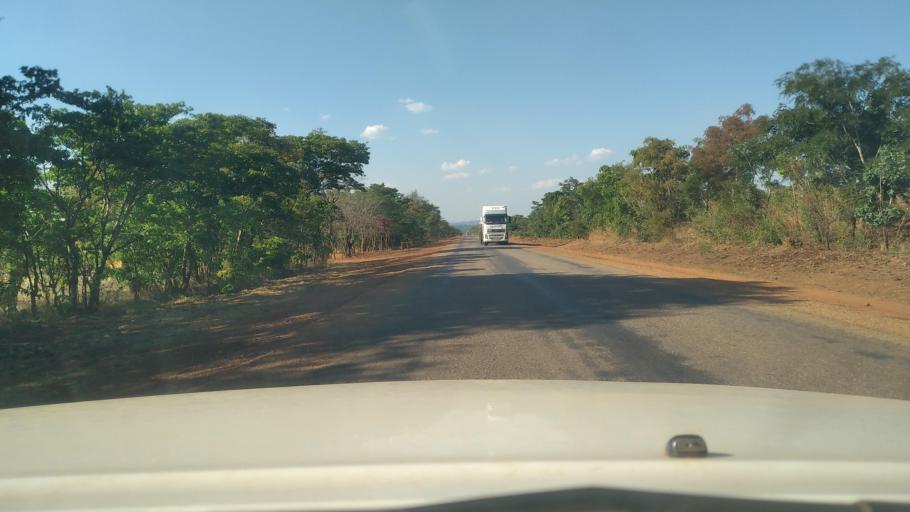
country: ZM
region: Northern
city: Mpika
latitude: -11.7723
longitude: 31.4619
